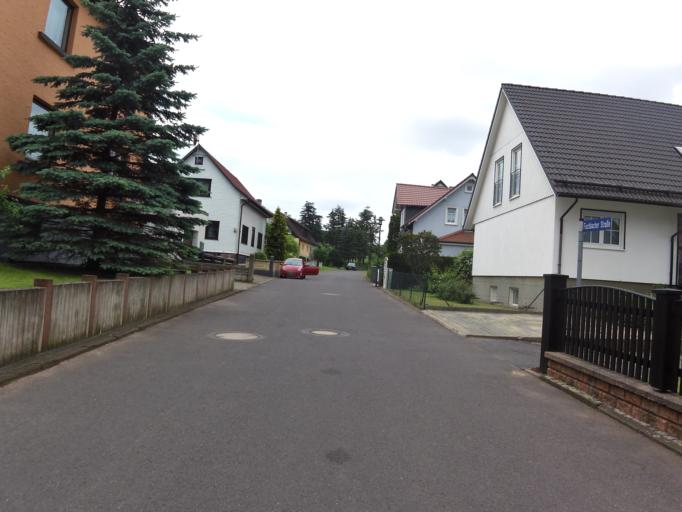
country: DE
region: Thuringia
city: Tabarz
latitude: 50.8798
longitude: 10.4992
